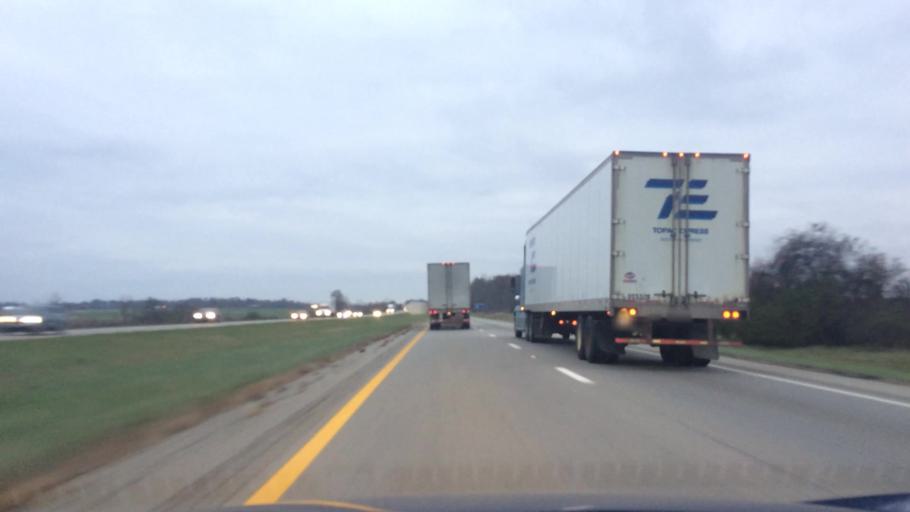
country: US
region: Ohio
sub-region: Union County
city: New California
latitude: 40.1736
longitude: -83.2436
